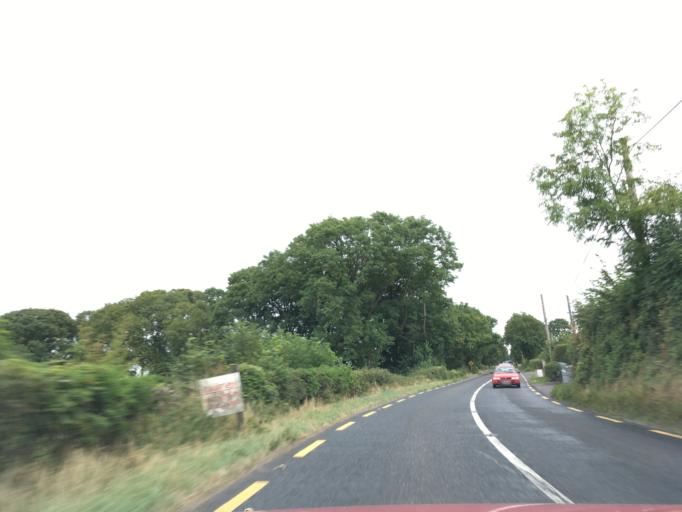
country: IE
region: Munster
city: Fethard
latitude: 52.4371
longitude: -7.7923
